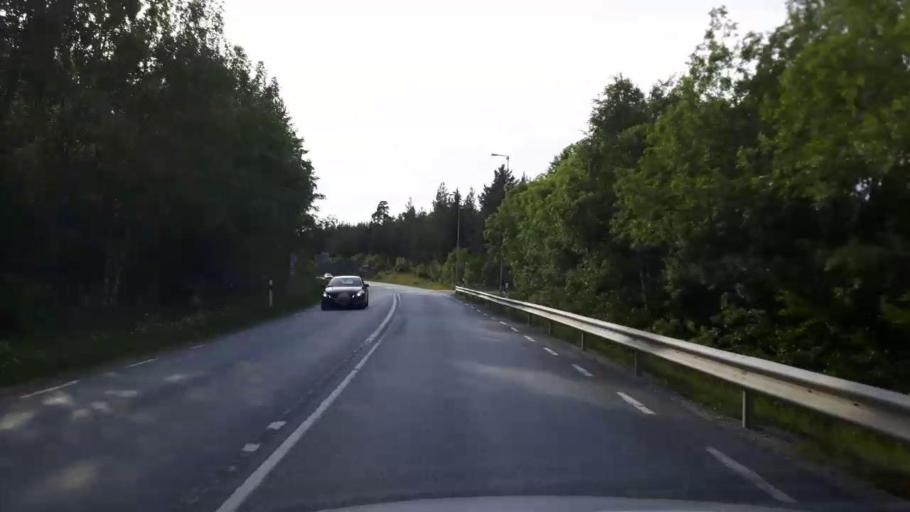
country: SE
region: Uppsala
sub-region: Habo Kommun
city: Balsta
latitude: 59.6520
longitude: 17.5590
